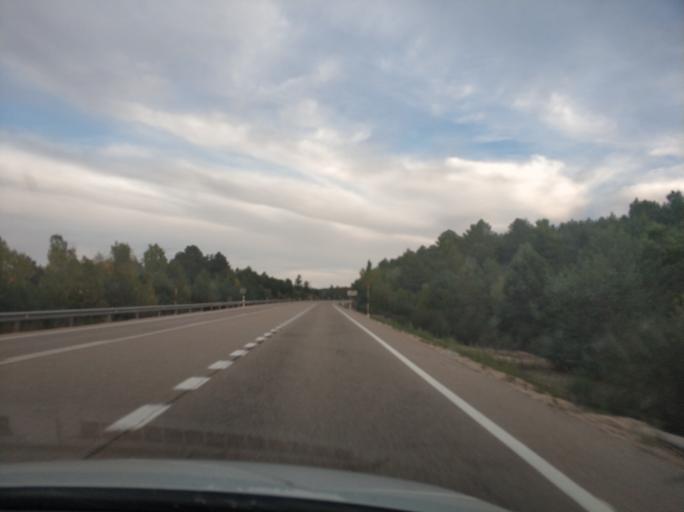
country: ES
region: Castille and Leon
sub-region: Provincia de Burgos
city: Pinilla de los Barruecos
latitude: 41.9039
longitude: -3.2743
